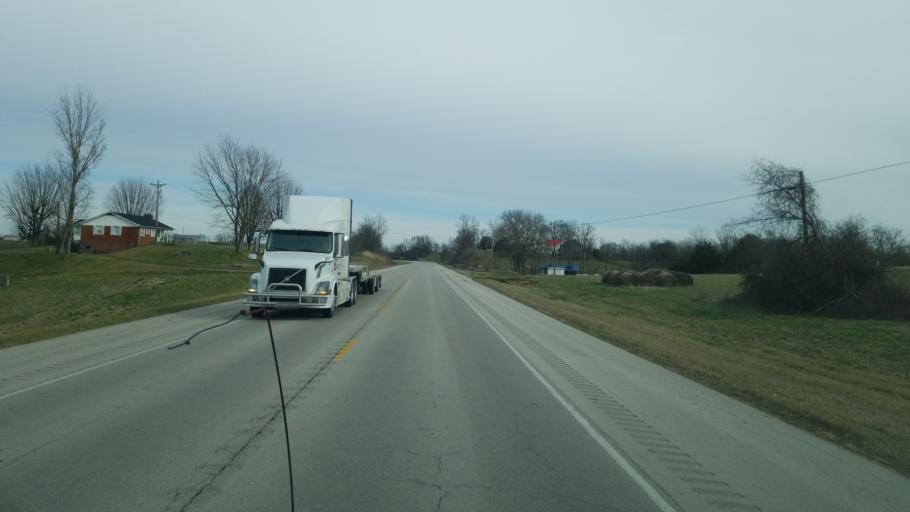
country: US
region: Kentucky
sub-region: Robertson County
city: Mount Olivet
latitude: 38.4619
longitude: -83.9233
